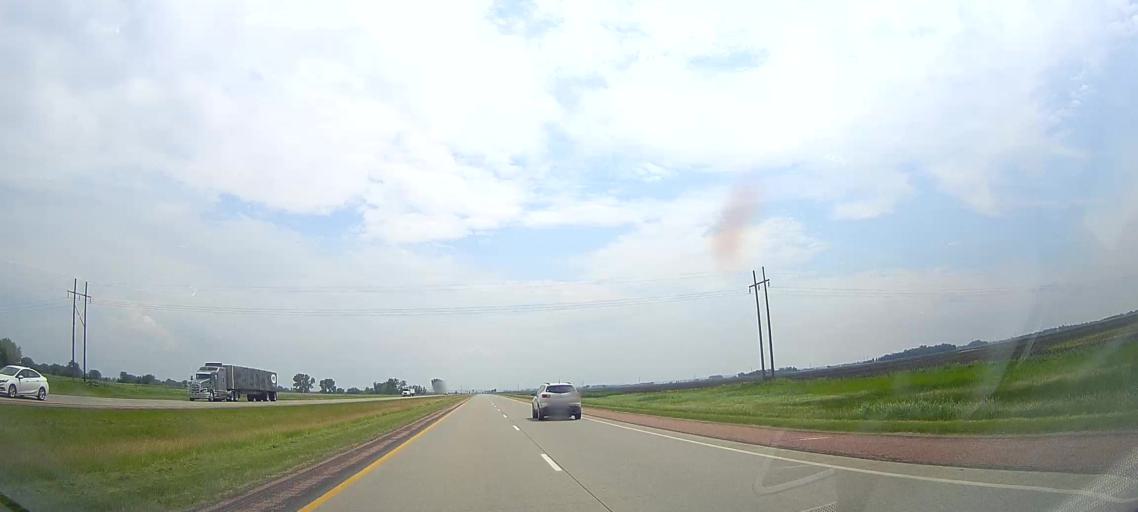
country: US
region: South Dakota
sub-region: Clay County
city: Vermillion
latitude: 42.8157
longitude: -96.7961
